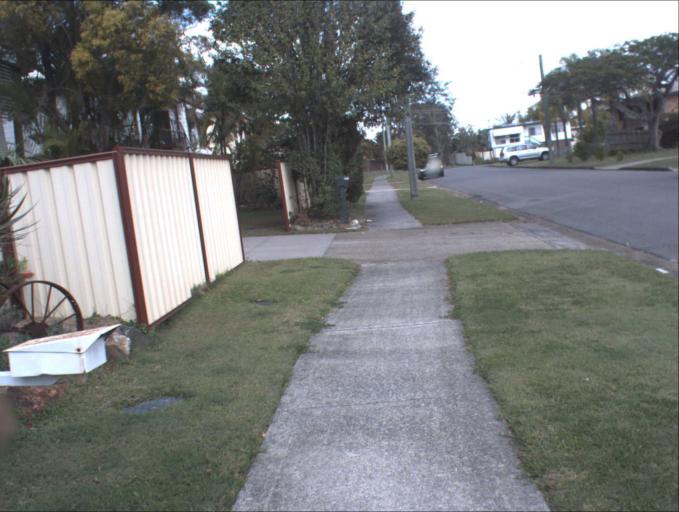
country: AU
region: Queensland
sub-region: Logan
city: Logan Reserve
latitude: -27.6819
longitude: 153.0830
